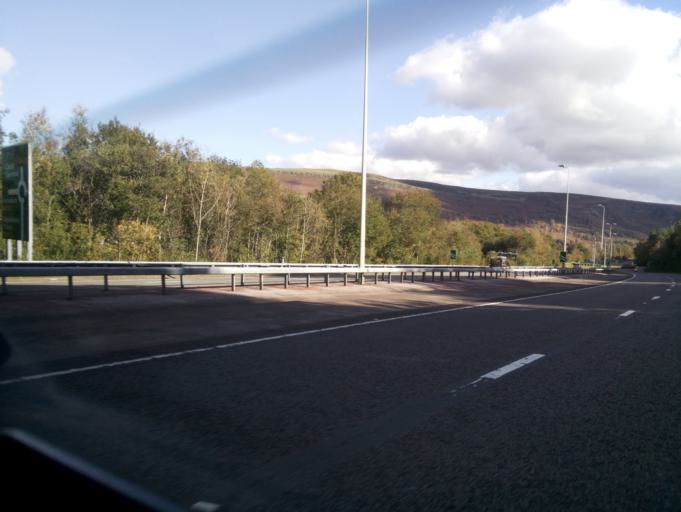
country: GB
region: Wales
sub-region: Merthyr Tydfil County Borough
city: Abercanaid
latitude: 51.7192
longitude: -3.3645
